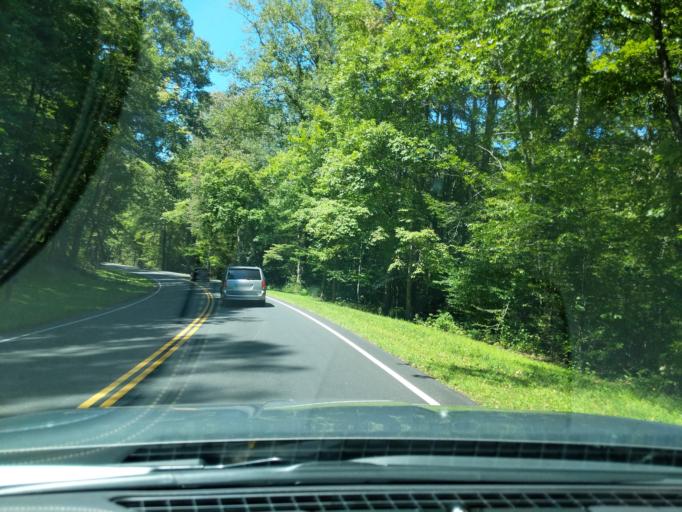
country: US
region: North Carolina
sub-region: Swain County
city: Cherokee
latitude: 35.5537
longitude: -83.3100
